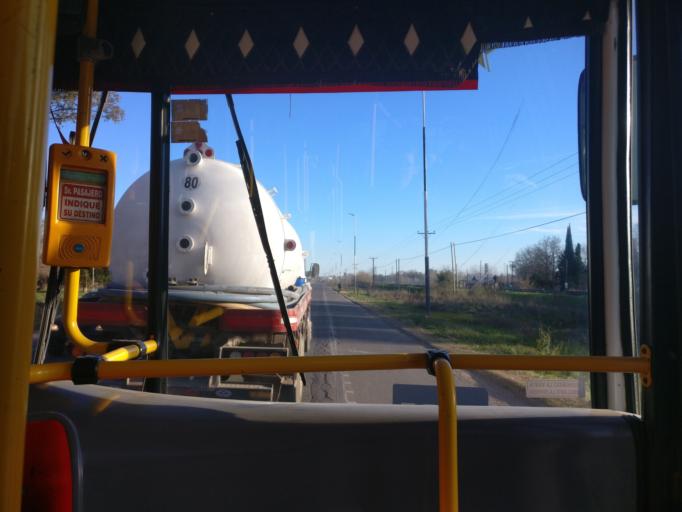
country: AR
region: Buenos Aires
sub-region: Partido de Ezeiza
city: Ezeiza
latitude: -34.9213
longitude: -58.6070
